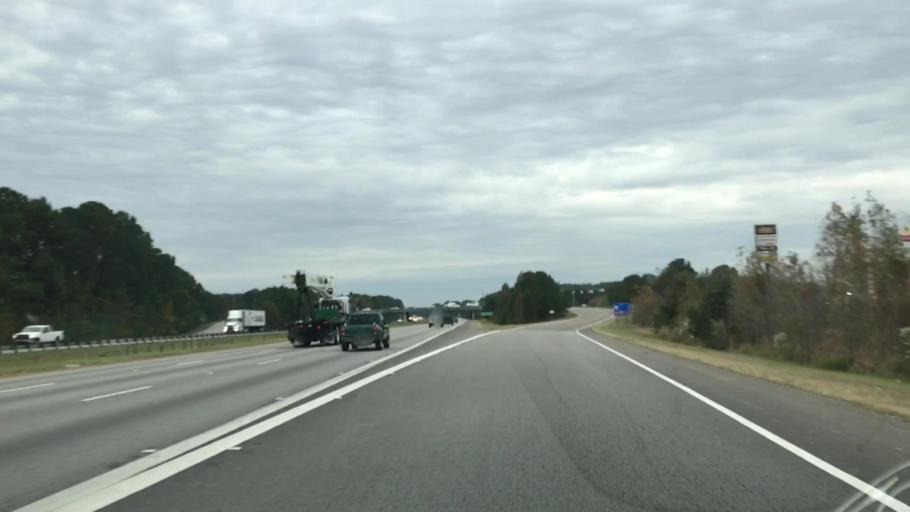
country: US
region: South Carolina
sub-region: Berkeley County
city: Ladson
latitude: 32.9960
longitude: -80.0908
